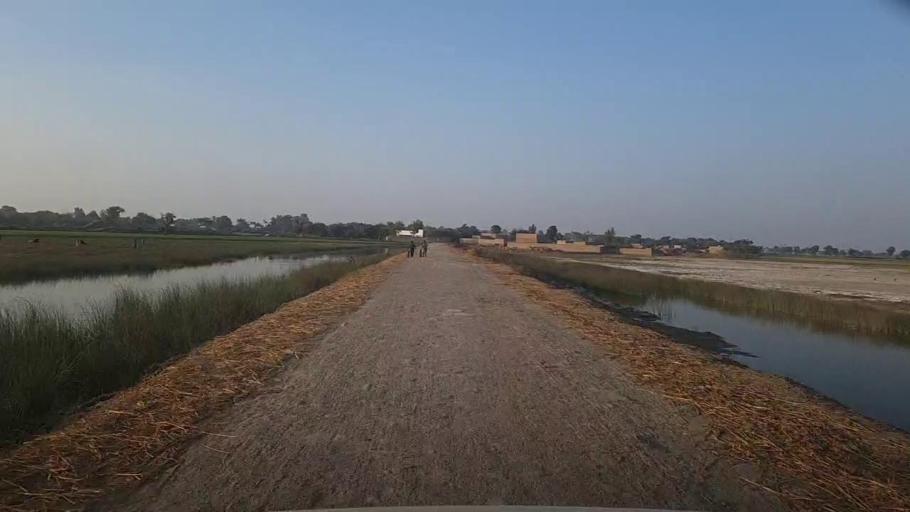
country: PK
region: Sindh
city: Mehar
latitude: 27.1959
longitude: 67.7821
